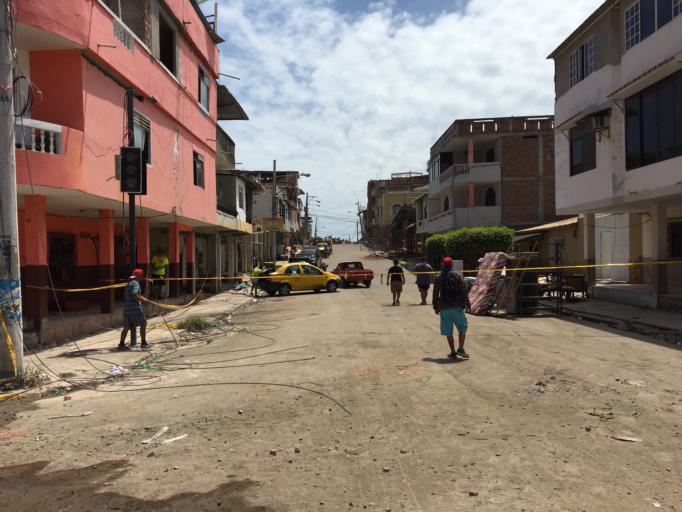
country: EC
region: Manabi
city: Manta
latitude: -0.9532
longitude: -80.7116
